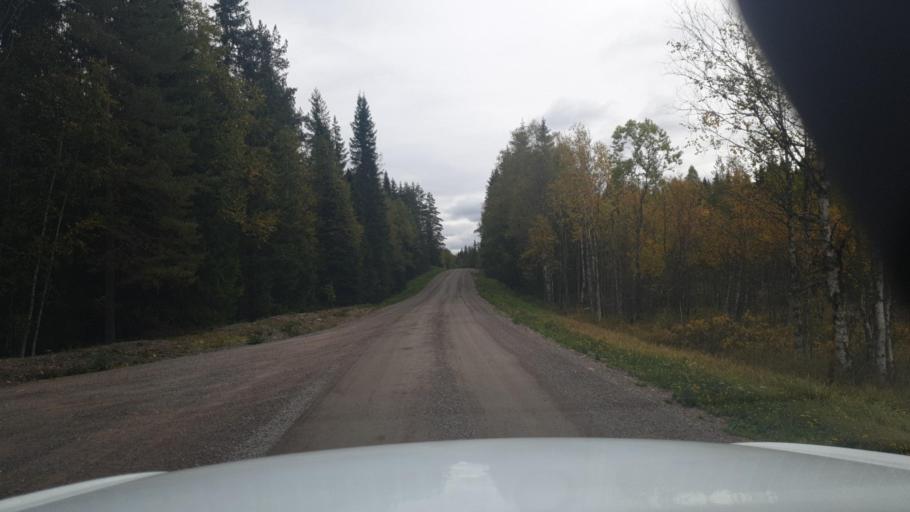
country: SE
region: Vaermland
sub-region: Eda Kommun
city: Charlottenberg
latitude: 60.0537
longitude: 12.5622
